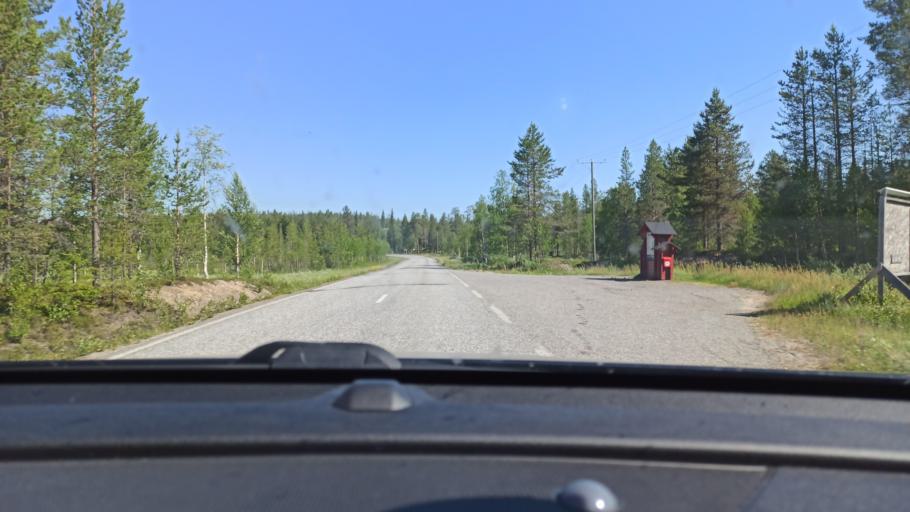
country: FI
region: Lapland
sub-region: Tunturi-Lappi
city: Kolari
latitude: 67.6317
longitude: 24.1582
